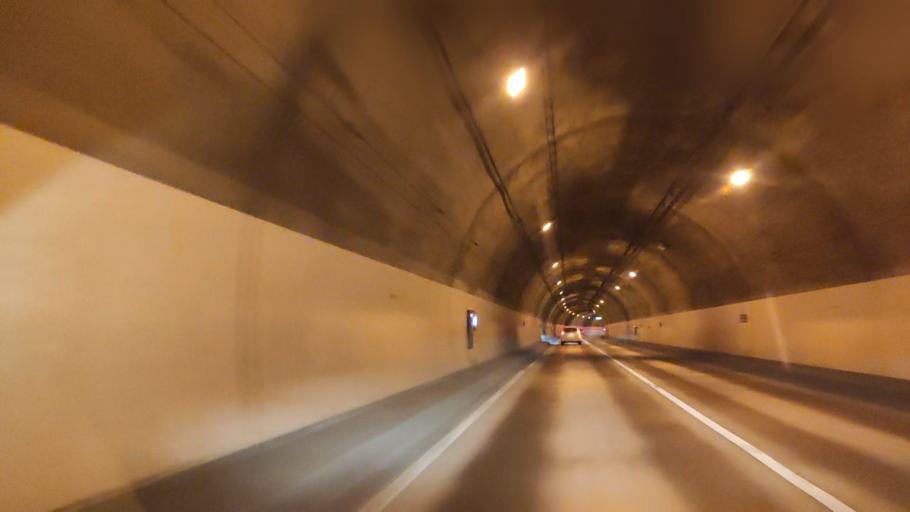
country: JP
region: Hokkaido
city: Ishikari
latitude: 43.4573
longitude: 141.4077
